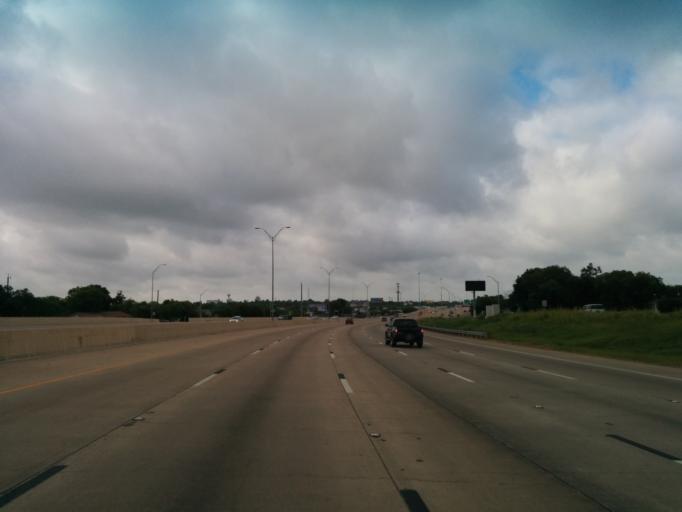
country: US
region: Texas
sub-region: Bexar County
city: Olmos Park
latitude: 29.4731
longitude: -98.5167
